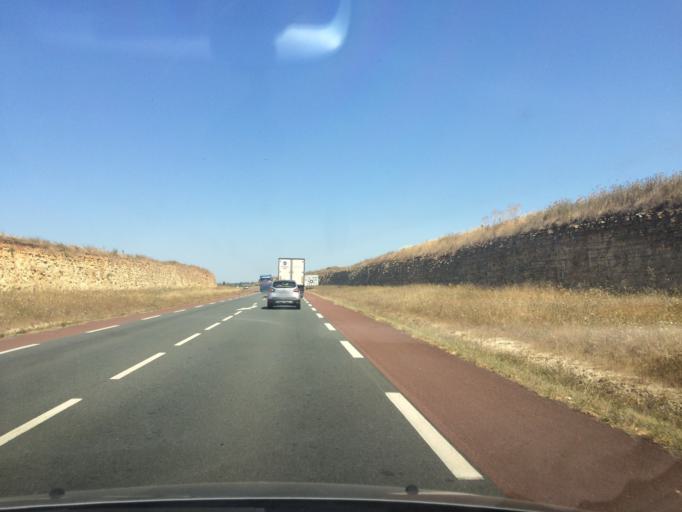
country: FR
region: Poitou-Charentes
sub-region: Departement de la Charente-Maritime
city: Esnandes
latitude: 46.2390
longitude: -1.0780
